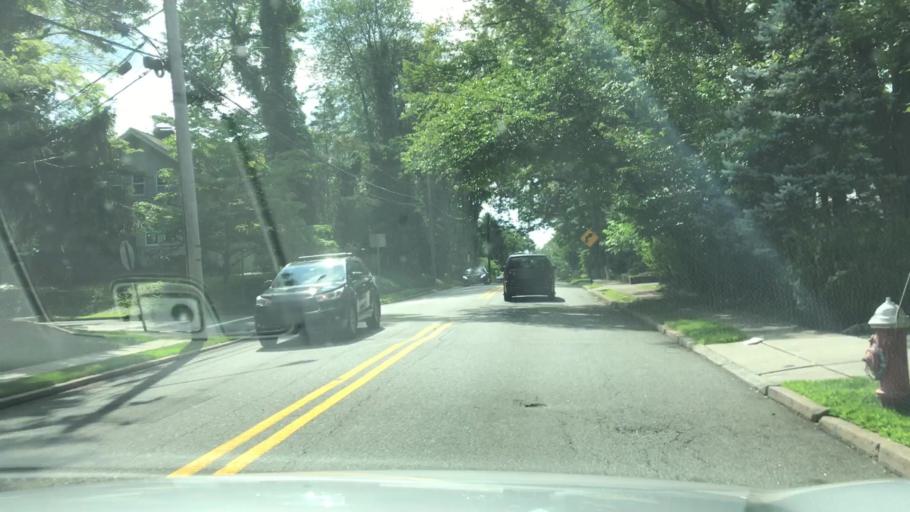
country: US
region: New Jersey
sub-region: Bergen County
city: Harrington Park
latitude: 40.9752
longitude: -73.9767
